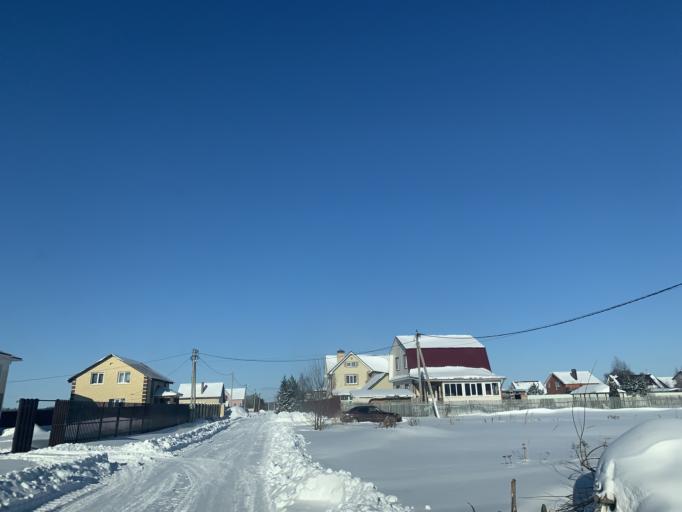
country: RU
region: Jaroslavl
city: Tunoshna
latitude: 57.6628
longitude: 40.0665
